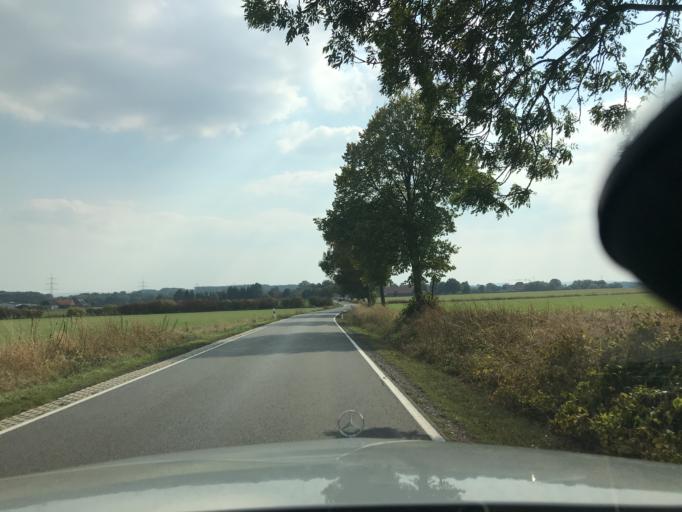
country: DE
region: North Rhine-Westphalia
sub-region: Regierungsbezirk Arnsberg
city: Werl
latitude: 51.6088
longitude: 7.8747
